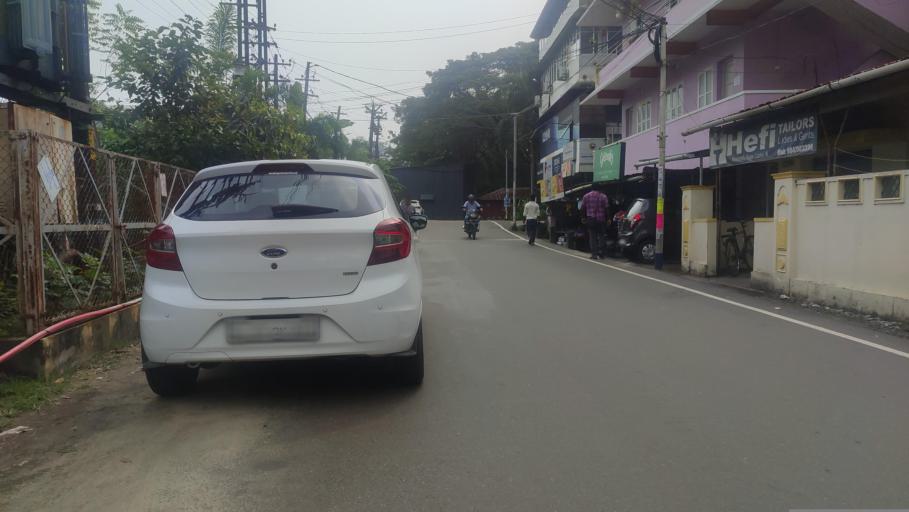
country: IN
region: Kerala
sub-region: Ernakulam
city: Cochin
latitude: 9.9597
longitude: 76.2984
